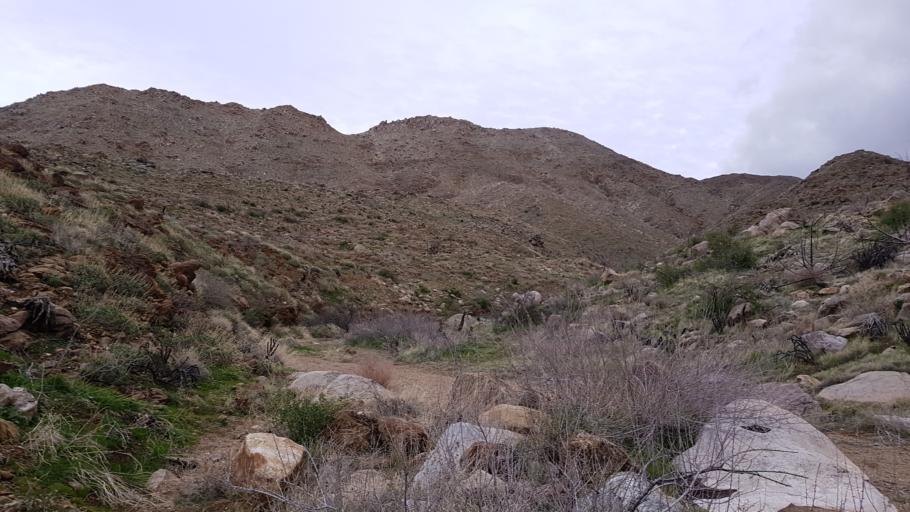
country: US
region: California
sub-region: San Diego County
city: Julian
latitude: 33.1285
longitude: -116.4729
